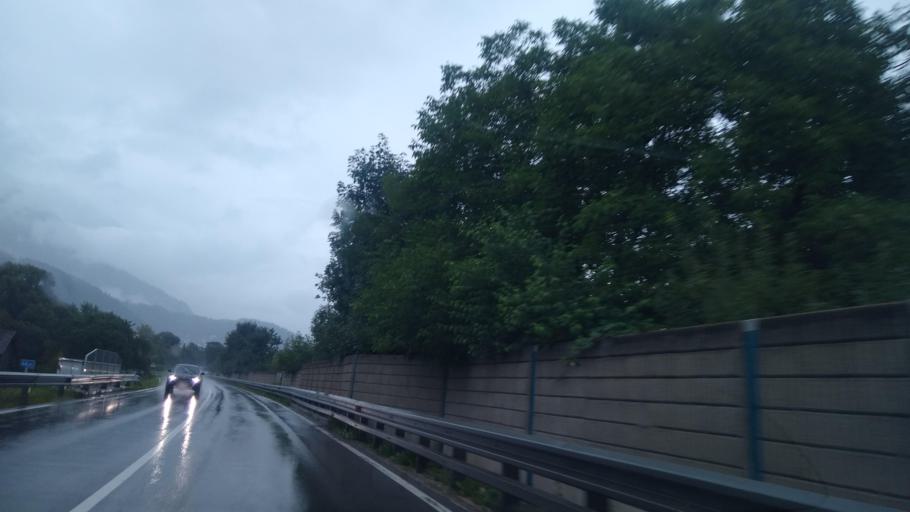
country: AT
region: Tyrol
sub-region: Politischer Bezirk Schwaz
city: Buch bei Jenbach
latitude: 47.3756
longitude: 11.7498
